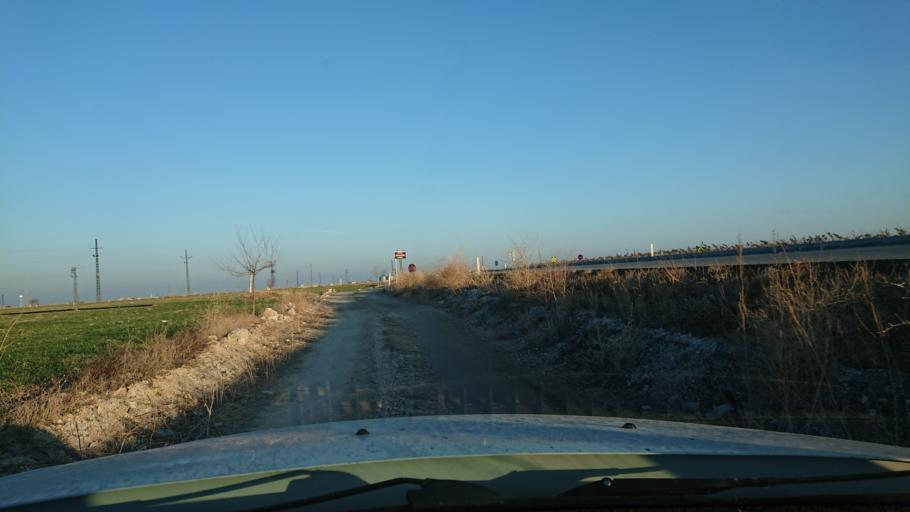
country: TR
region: Aksaray
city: Sultanhani
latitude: 38.2518
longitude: 33.5105
